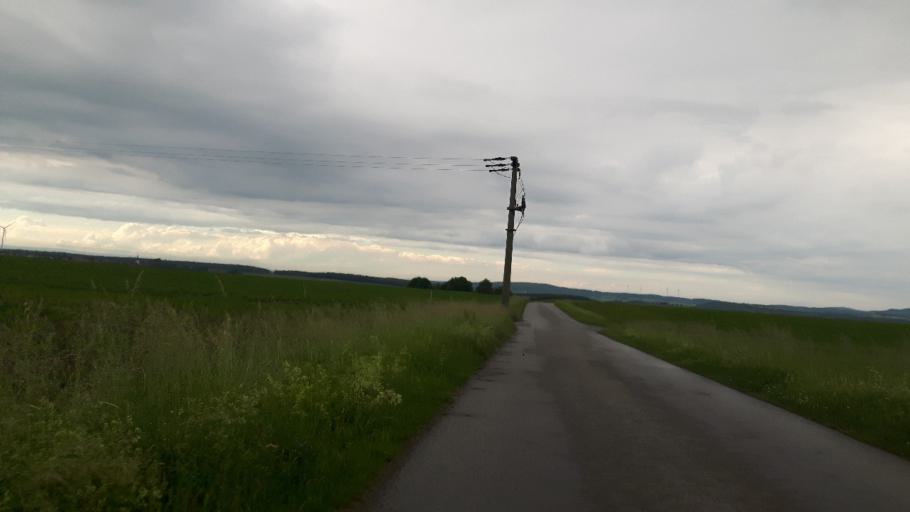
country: DE
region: Bavaria
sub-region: Regierungsbezirk Unterfranken
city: Stadtlauringen
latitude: 50.1449
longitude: 10.3498
